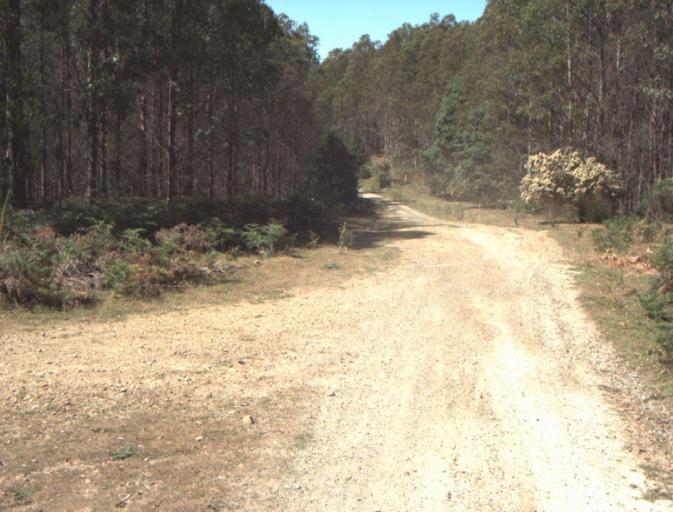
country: AU
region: Tasmania
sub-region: Dorset
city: Scottsdale
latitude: -41.2582
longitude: 147.3470
